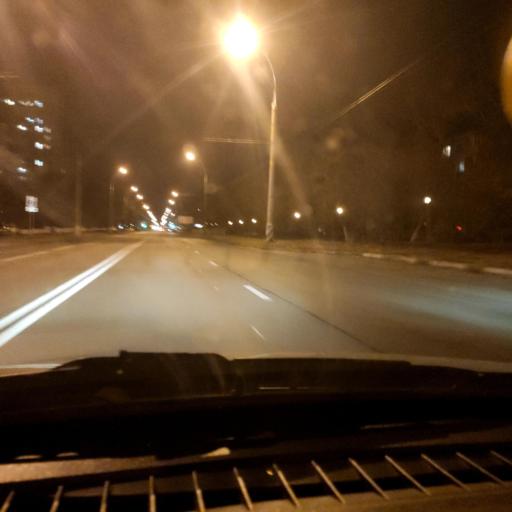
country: RU
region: Samara
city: Tol'yatti
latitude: 53.5057
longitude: 49.2878
